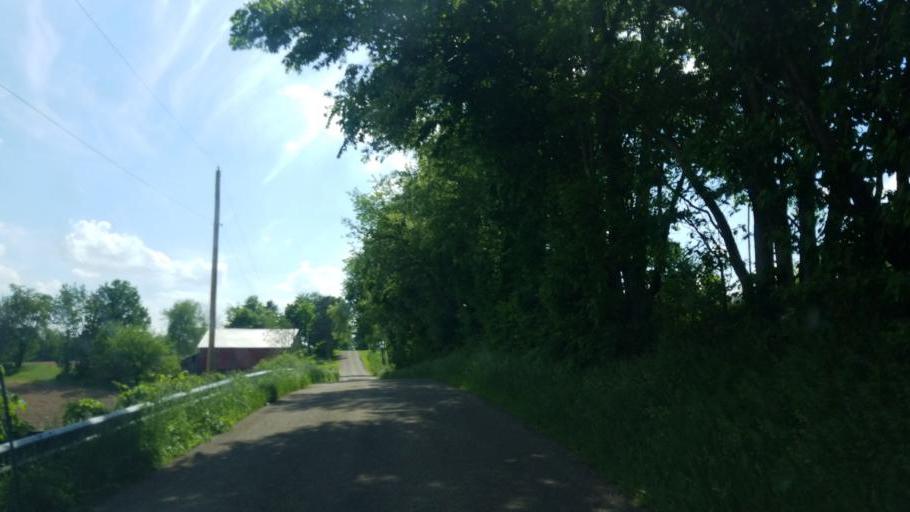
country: US
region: Ohio
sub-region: Sandusky County
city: Bellville
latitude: 40.6620
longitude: -82.5310
